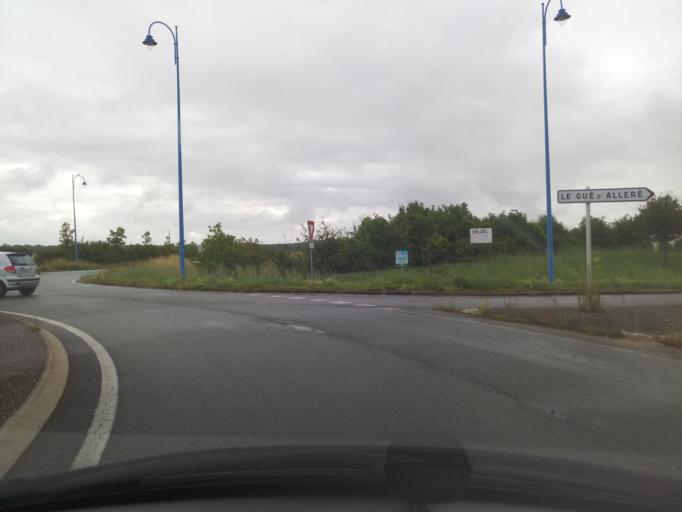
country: FR
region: Poitou-Charentes
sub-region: Departement de la Charente-Maritime
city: Courcon
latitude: 46.1950
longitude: -0.8684
